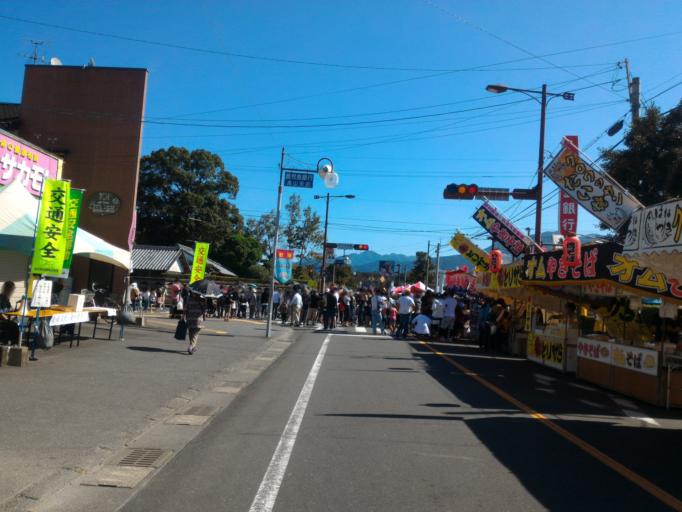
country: JP
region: Kagoshima
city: Kanoya
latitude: 31.3469
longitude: 130.9473
